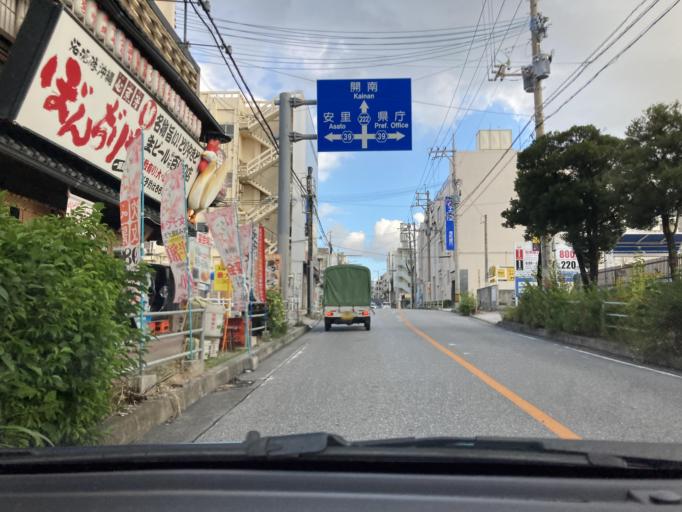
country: JP
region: Okinawa
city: Naha-shi
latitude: 26.2159
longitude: 127.6841
